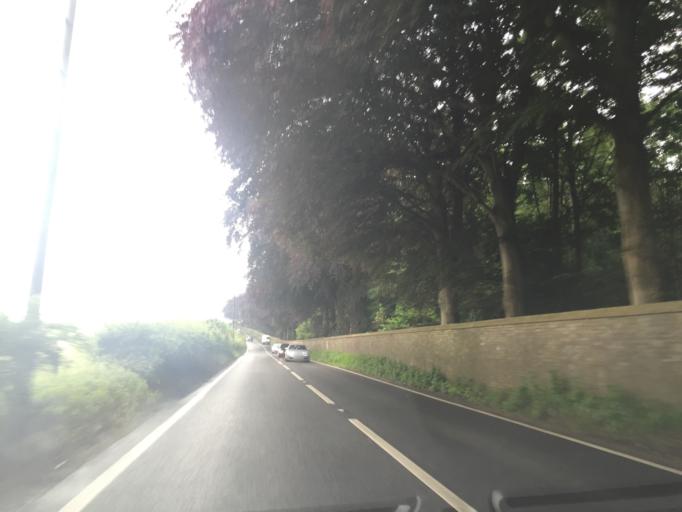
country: GB
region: England
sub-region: Dorset
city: Lytchett Matravers
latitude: 50.7891
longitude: -2.0904
